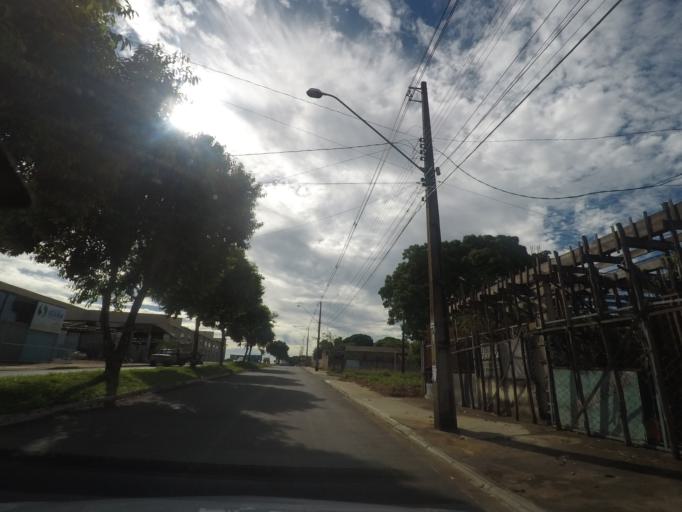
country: BR
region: Goias
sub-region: Aparecida De Goiania
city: Aparecida de Goiania
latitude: -16.8190
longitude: -49.2980
